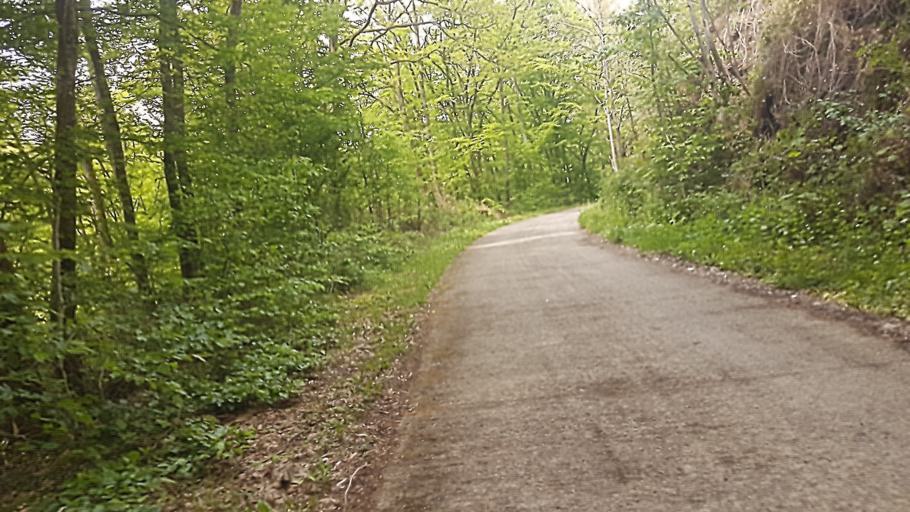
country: BE
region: Wallonia
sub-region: Province de Namur
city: Couvin
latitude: 50.0459
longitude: 4.5952
